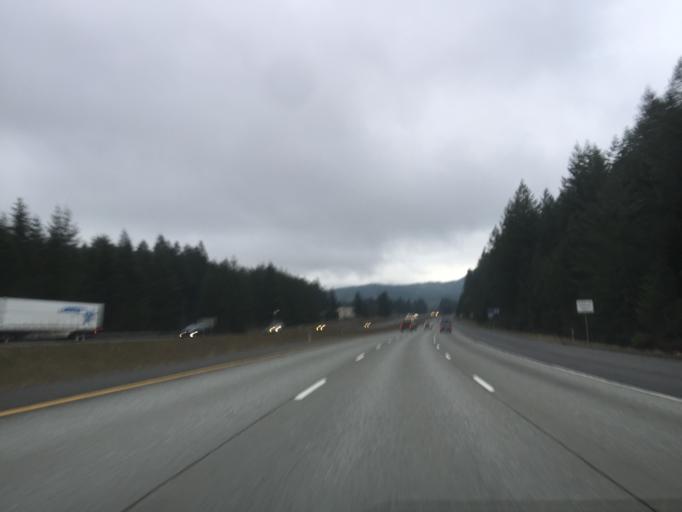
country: US
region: Washington
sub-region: King County
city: Tanner
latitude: 47.4729
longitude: -121.7406
